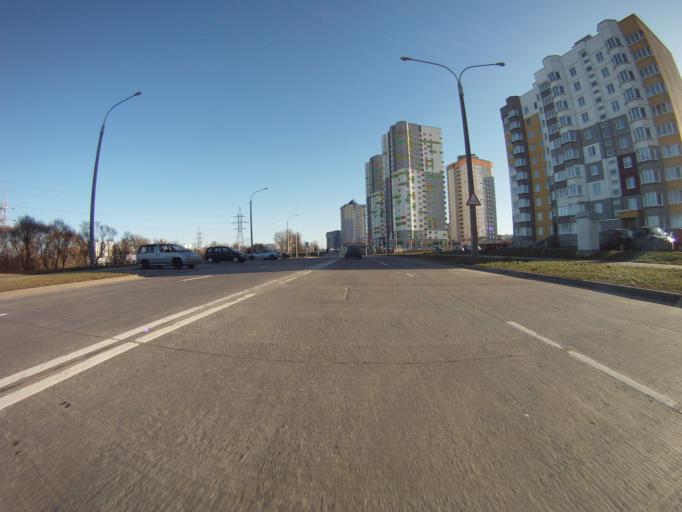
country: BY
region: Minsk
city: Novoye Medvezhino
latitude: 53.8751
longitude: 27.4742
